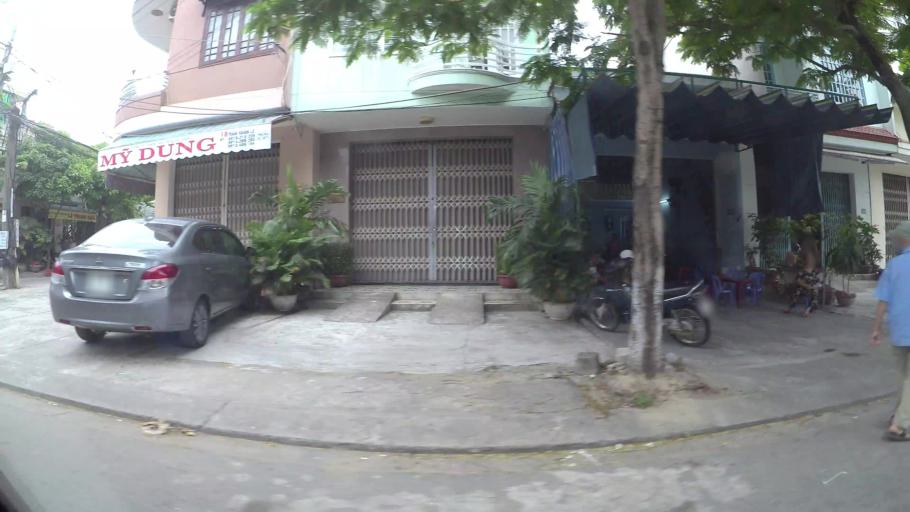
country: VN
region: Da Nang
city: Thanh Khe
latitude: 16.0610
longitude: 108.1859
